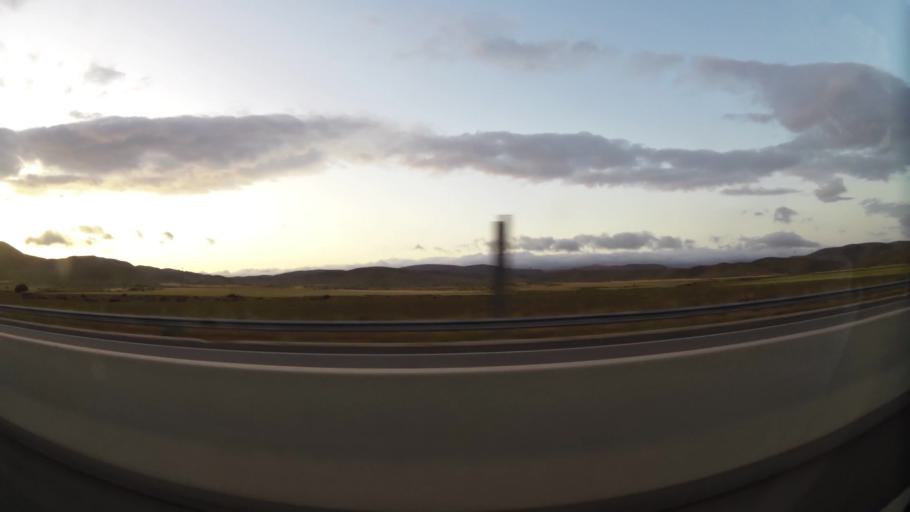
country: MA
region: Oriental
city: El Aioun
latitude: 34.6050
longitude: -2.6070
